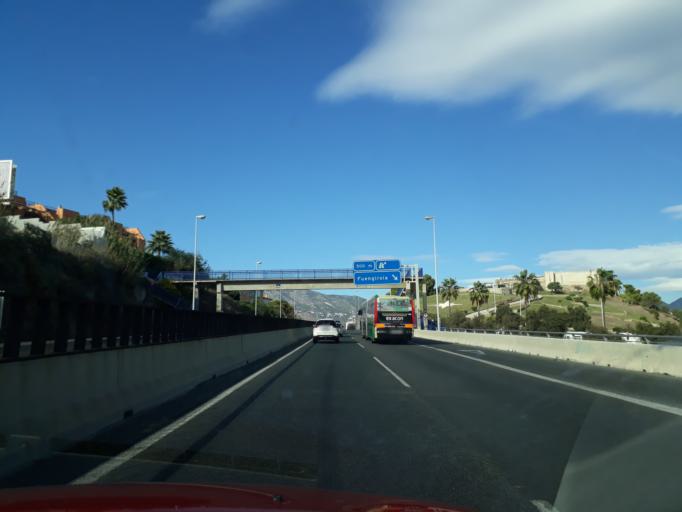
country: ES
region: Andalusia
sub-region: Provincia de Malaga
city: Fuengirola
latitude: 36.5229
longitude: -4.6301
